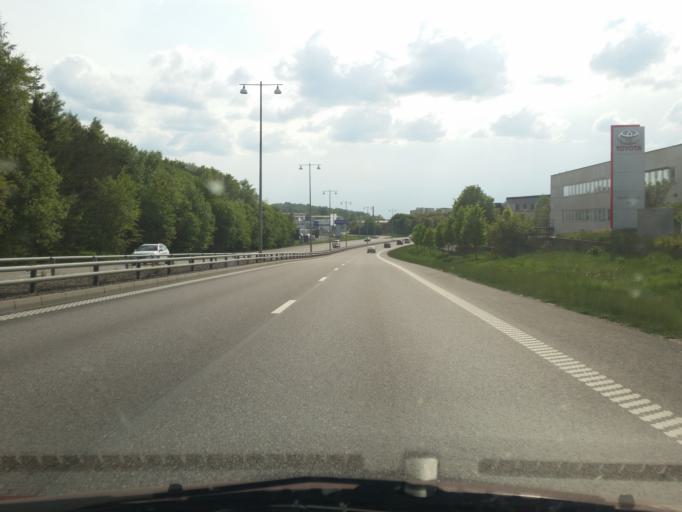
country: SE
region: Vaestra Goetaland
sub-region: Boras Kommun
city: Ganghester
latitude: 57.7251
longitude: 12.9971
